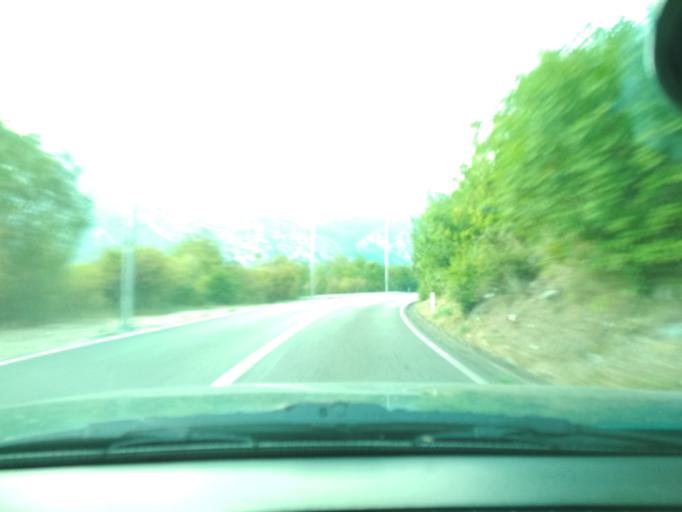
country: ME
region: Kotor
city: Risan
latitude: 42.4951
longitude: 18.6913
